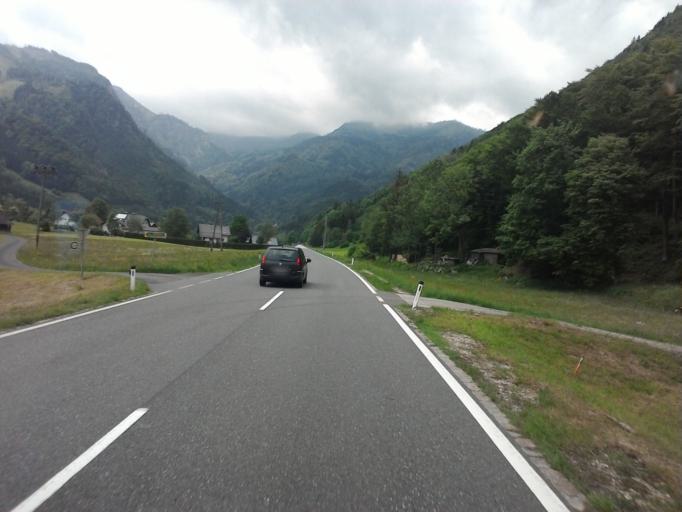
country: AT
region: Upper Austria
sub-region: Politischer Bezirk Steyr-Land
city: Weyer
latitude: 47.8571
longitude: 14.6312
